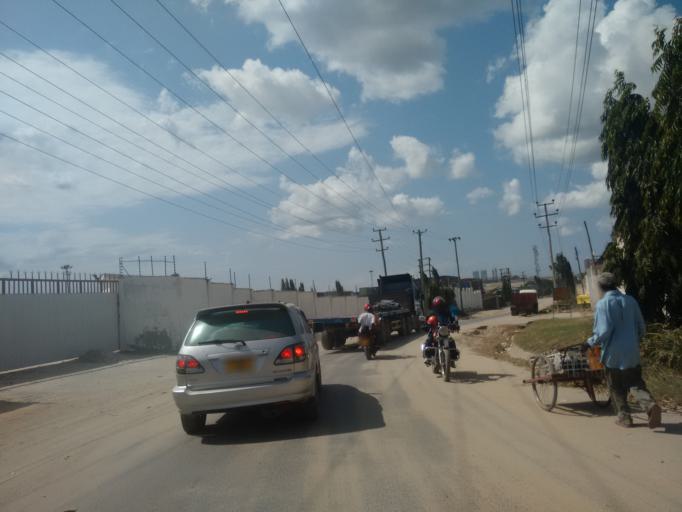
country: TZ
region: Dar es Salaam
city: Dar es Salaam
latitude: -6.8441
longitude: 39.2543
